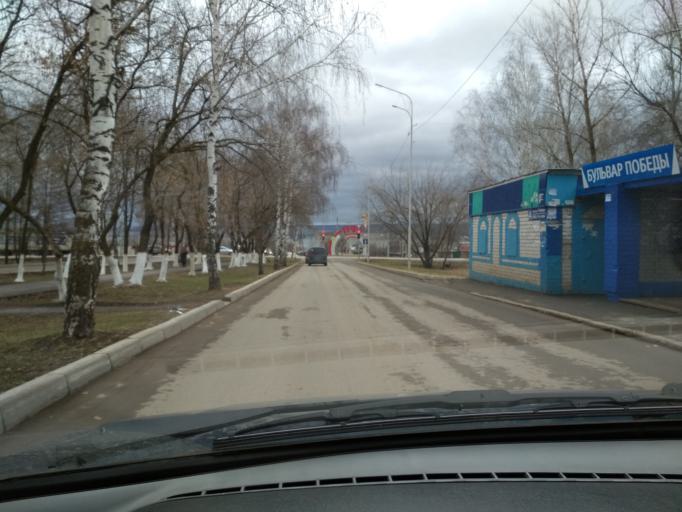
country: RU
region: Tatarstan
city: Zainsk
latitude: 55.2829
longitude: 52.0074
